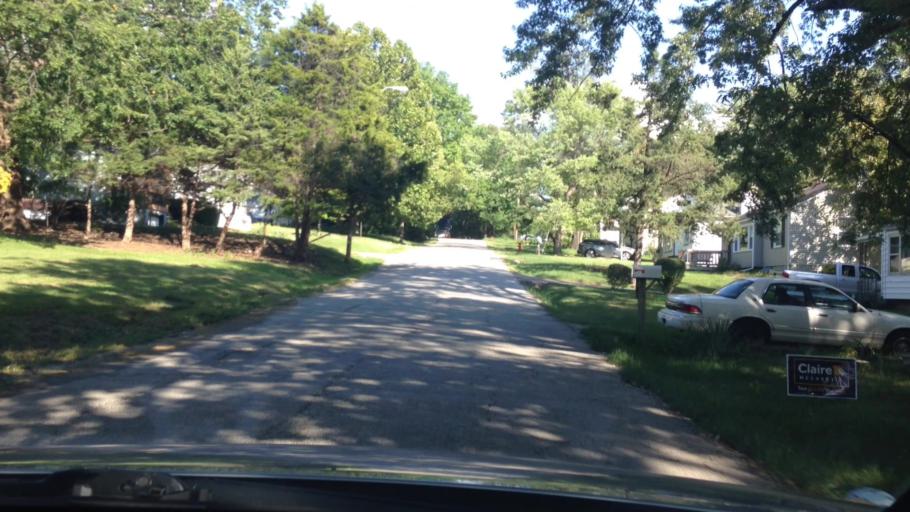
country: US
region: Kansas
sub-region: Johnson County
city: Leawood
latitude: 38.9768
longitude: -94.5804
